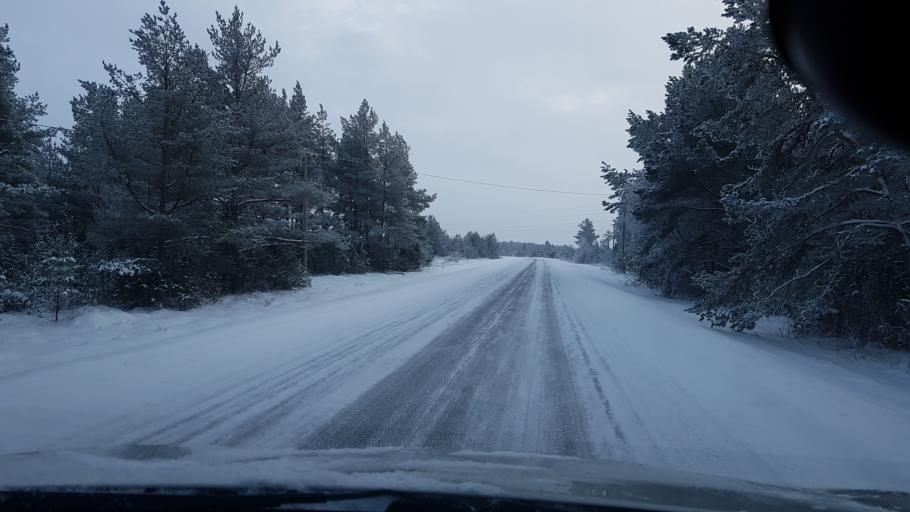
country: EE
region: Harju
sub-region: Keila linn
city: Keila
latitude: 59.3526
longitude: 24.4270
